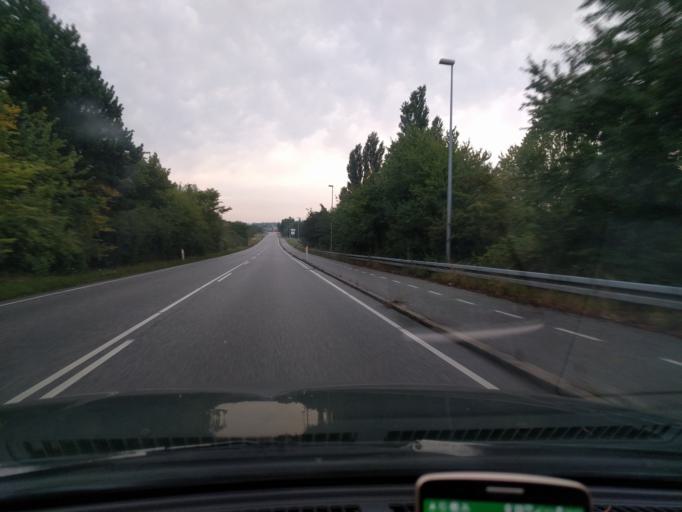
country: DK
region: Zealand
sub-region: Guldborgsund Kommune
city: Norre Alslev
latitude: 54.9509
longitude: 11.8670
